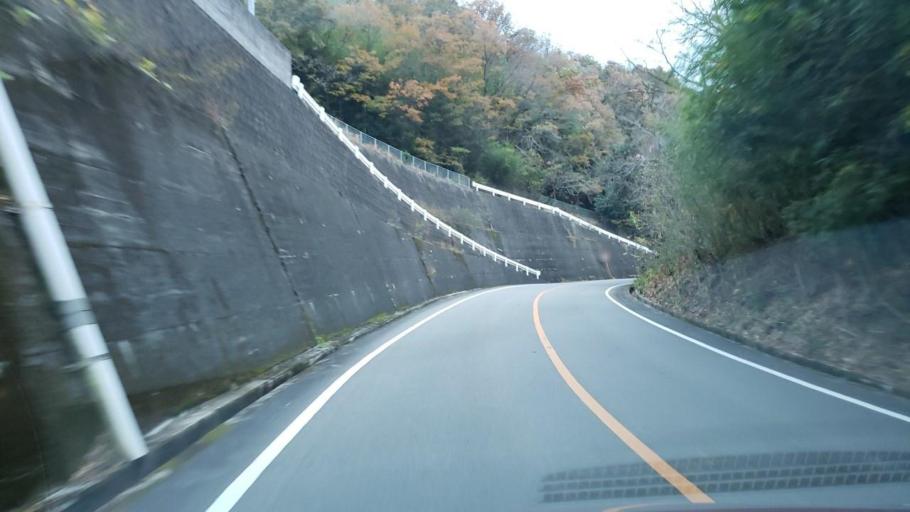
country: JP
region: Tokushima
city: Wakimachi
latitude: 34.0879
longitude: 134.1792
